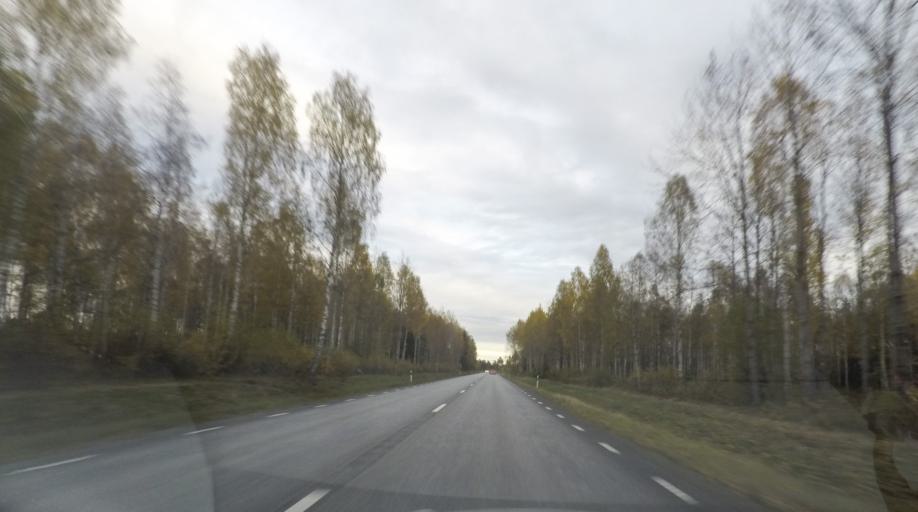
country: SE
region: OErebro
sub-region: Nora Kommun
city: Nora
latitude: 59.4810
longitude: 15.0856
